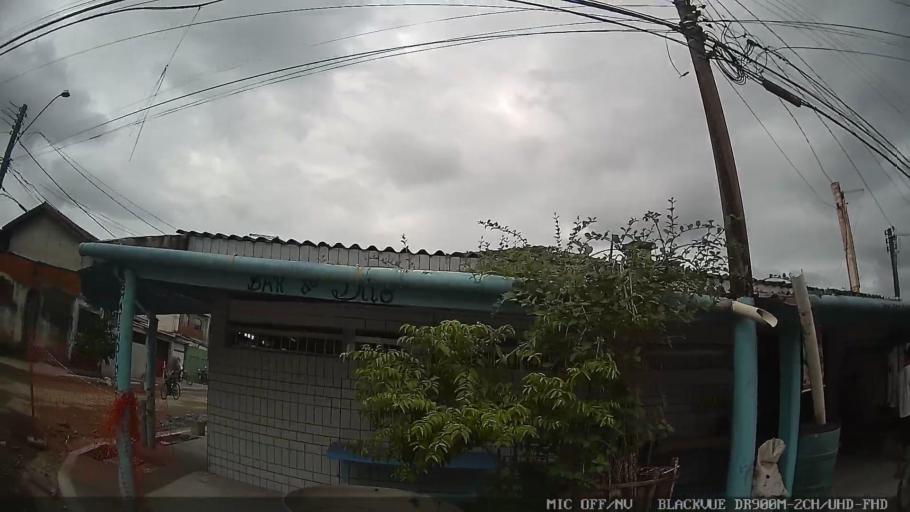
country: BR
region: Sao Paulo
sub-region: Guaruja
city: Guaruja
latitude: -23.9973
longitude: -46.2908
